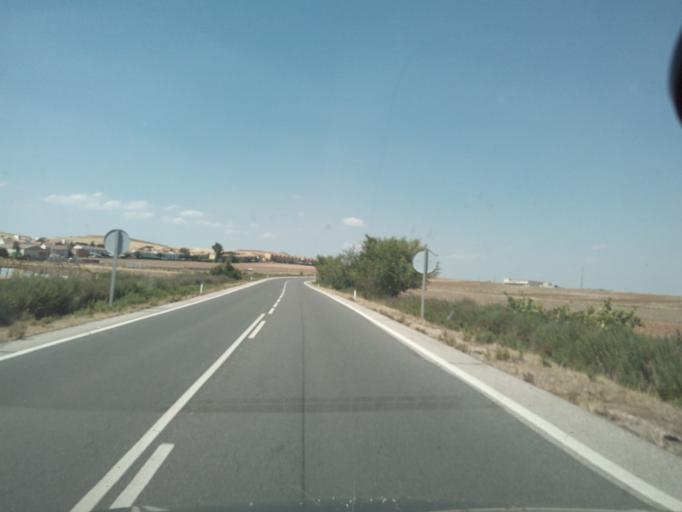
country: ES
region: Madrid
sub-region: Provincia de Madrid
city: Ajalvir
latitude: 40.5297
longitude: -3.4759
